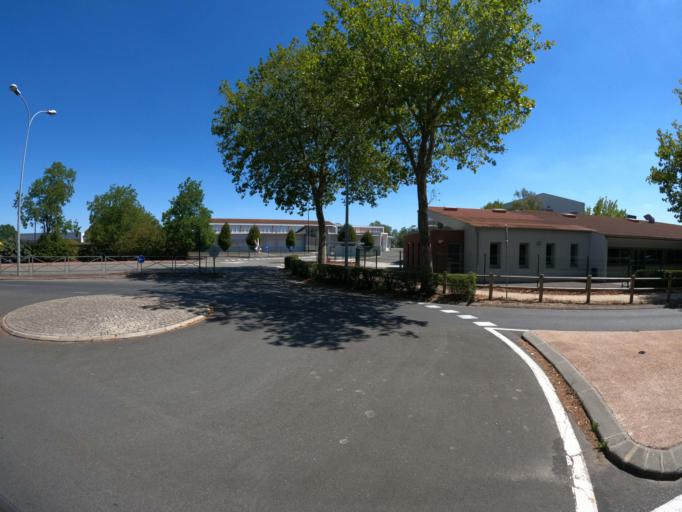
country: FR
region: Pays de la Loire
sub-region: Departement de la Vendee
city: Challans
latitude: 46.8391
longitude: -1.8656
